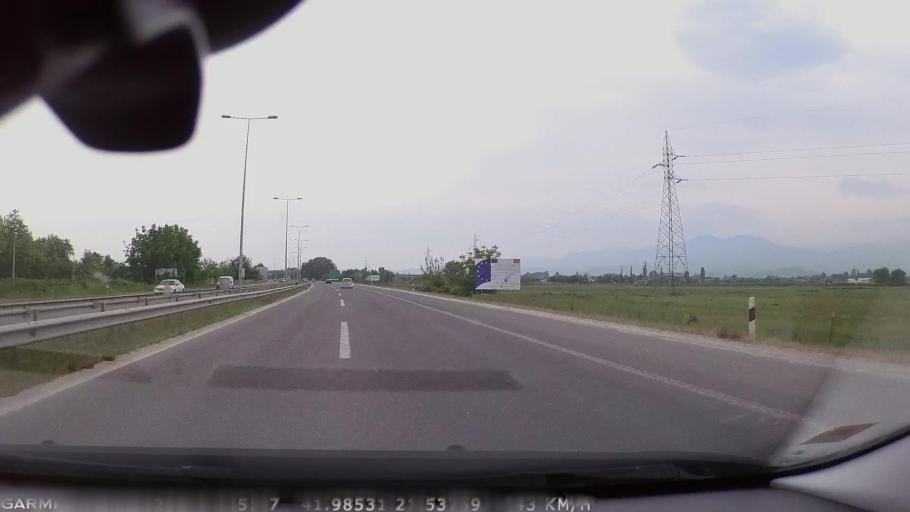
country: MK
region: Ilinden
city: Jurumleri
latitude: 41.9839
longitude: 21.5386
